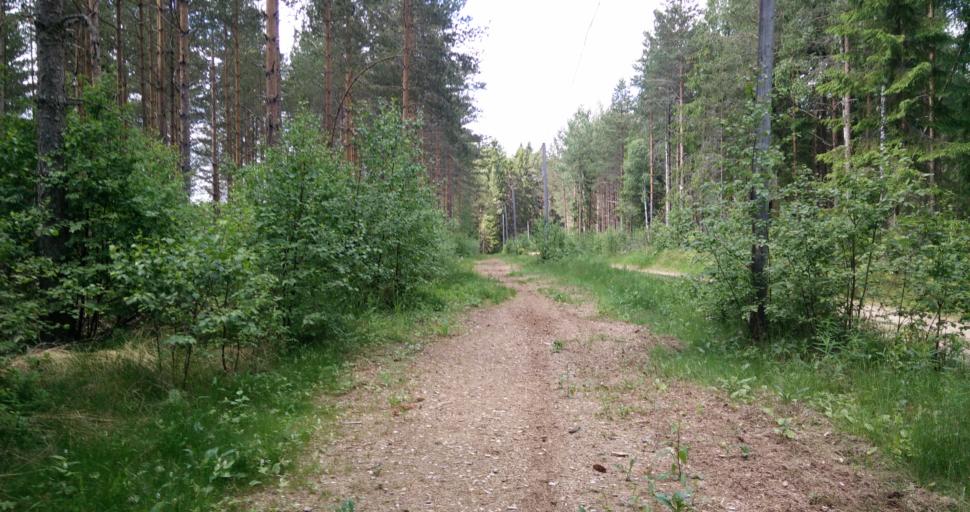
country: SE
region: Vaermland
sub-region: Hagfors Kommun
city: Hagfors
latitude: 60.0120
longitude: 13.5709
